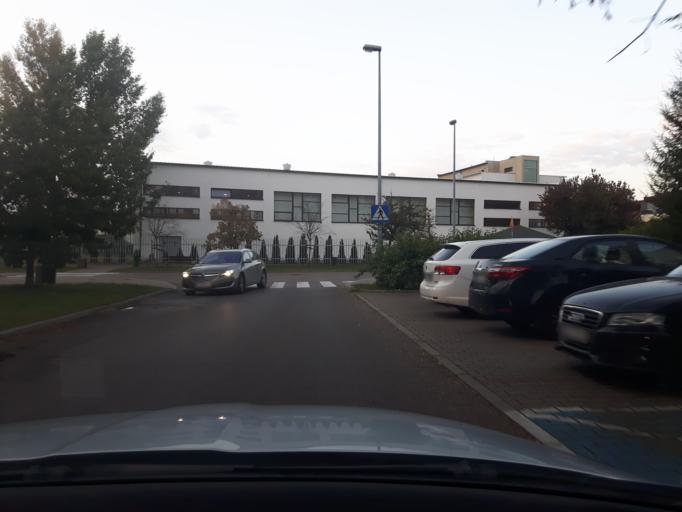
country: PL
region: Masovian Voivodeship
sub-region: Warszawa
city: Kabaty
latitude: 52.1320
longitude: 21.0605
